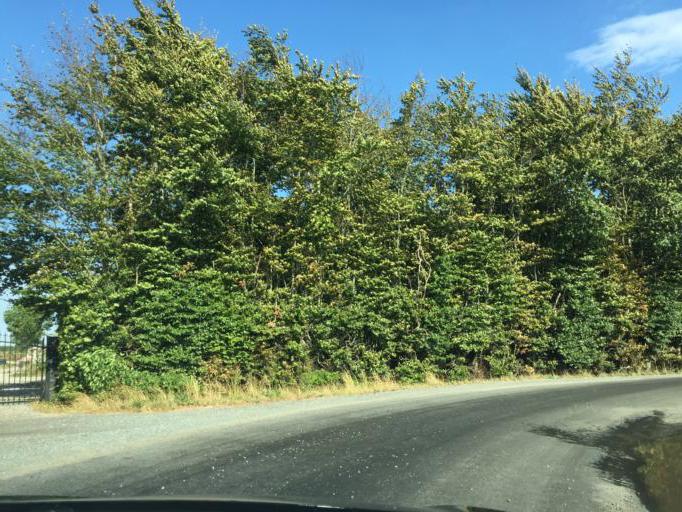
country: DK
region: South Denmark
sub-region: Faaborg-Midtfyn Kommune
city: Arslev
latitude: 55.3081
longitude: 10.4327
